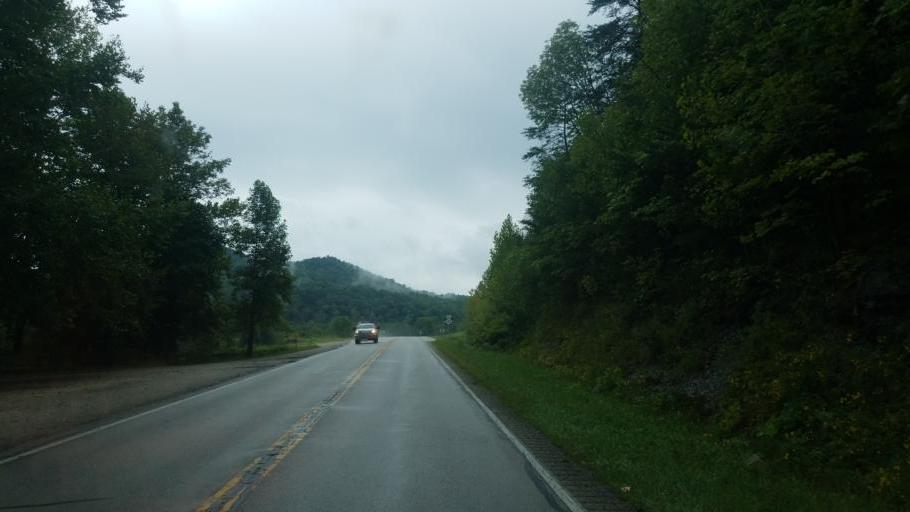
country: US
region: Kentucky
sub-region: Rowan County
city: Morehead
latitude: 38.1500
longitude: -83.5035
